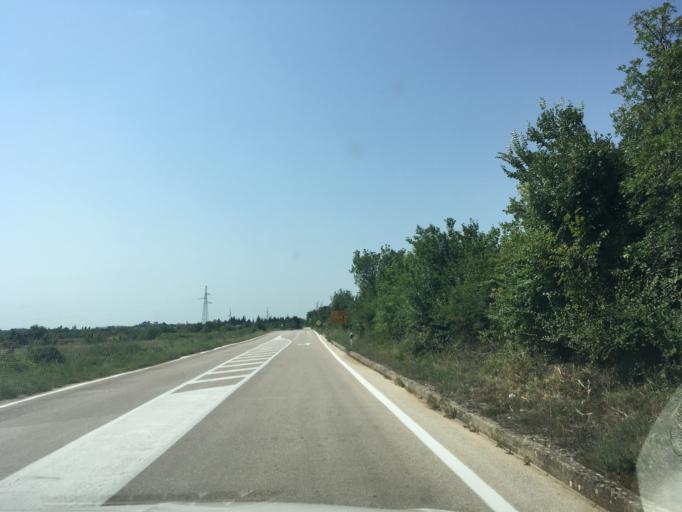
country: HR
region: Zadarska
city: Benkovac
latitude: 44.0232
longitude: 15.6345
